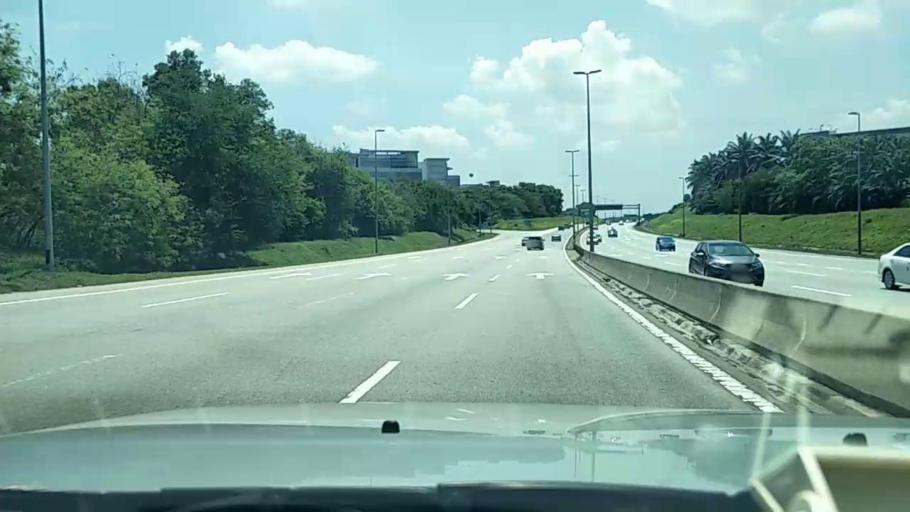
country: MY
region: Putrajaya
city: Putrajaya
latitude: 2.9330
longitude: 101.6585
